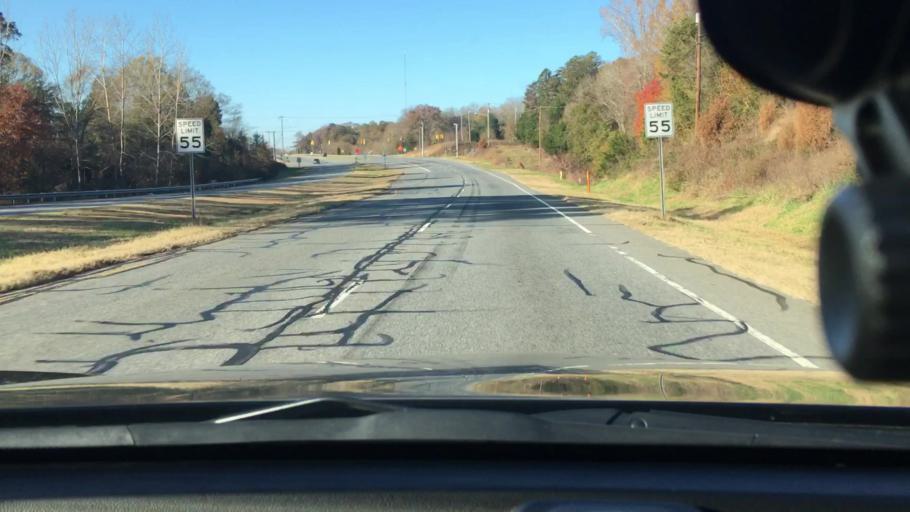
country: US
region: North Carolina
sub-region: Cabarrus County
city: Concord
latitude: 35.3684
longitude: -80.5755
